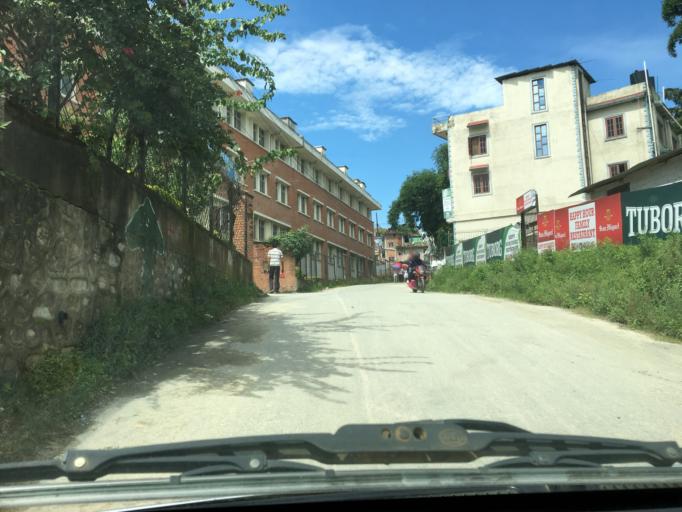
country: NP
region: Central Region
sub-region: Bagmati Zone
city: Kathmandu
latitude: 27.7321
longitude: 85.3780
